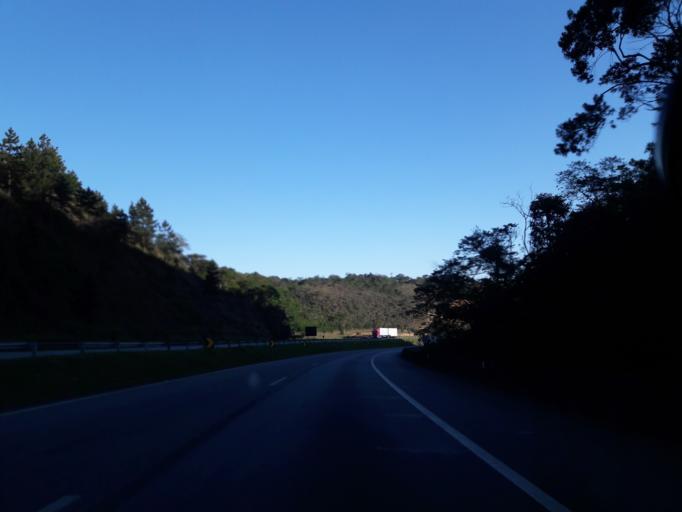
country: BR
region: Sao Paulo
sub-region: Juquitiba
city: Juquitiba
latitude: -23.9922
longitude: -47.1477
